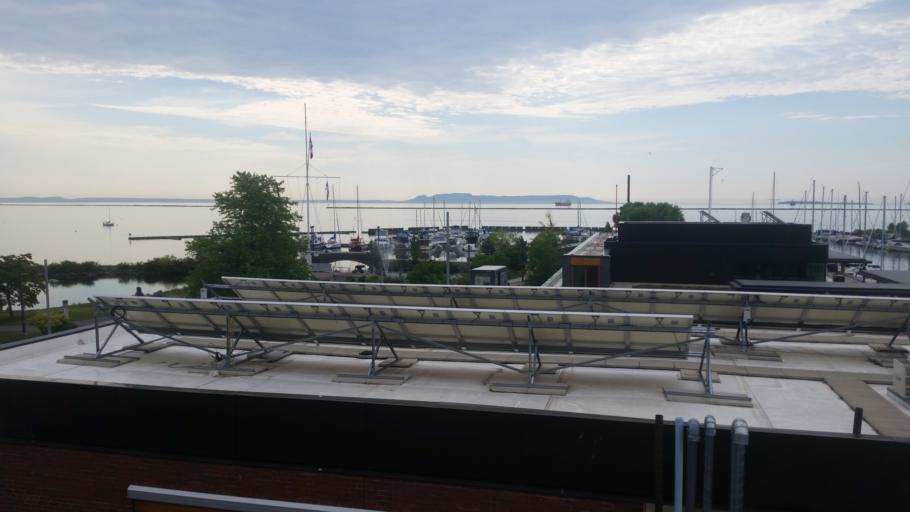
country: CA
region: Ontario
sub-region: Thunder Bay District
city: Thunder Bay
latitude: 48.4343
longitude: -89.2174
